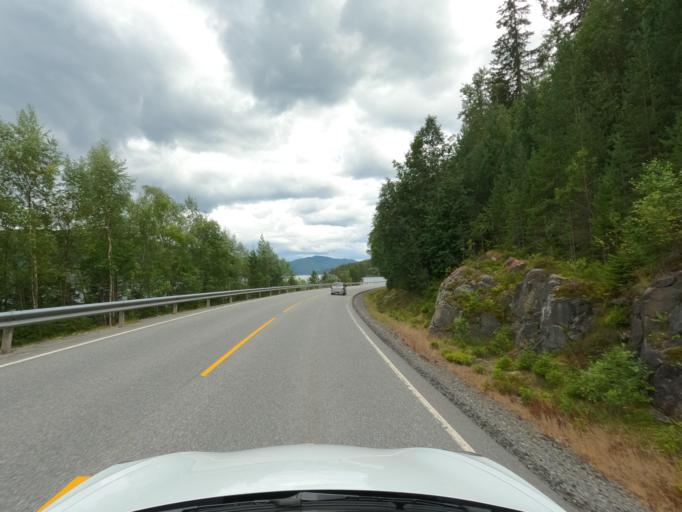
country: NO
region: Telemark
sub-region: Hjartdal
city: Sauland
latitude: 59.8673
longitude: 8.9325
